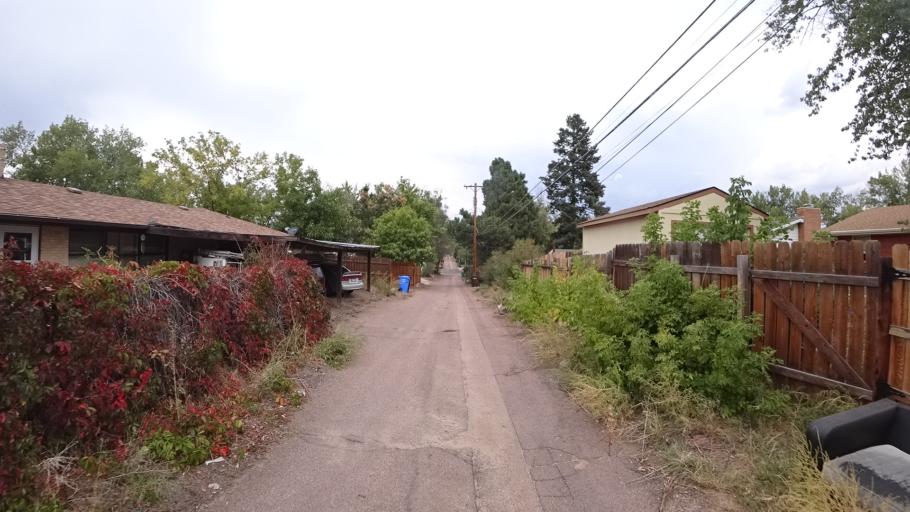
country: US
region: Colorado
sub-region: El Paso County
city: Colorado Springs
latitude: 38.8616
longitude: -104.7890
